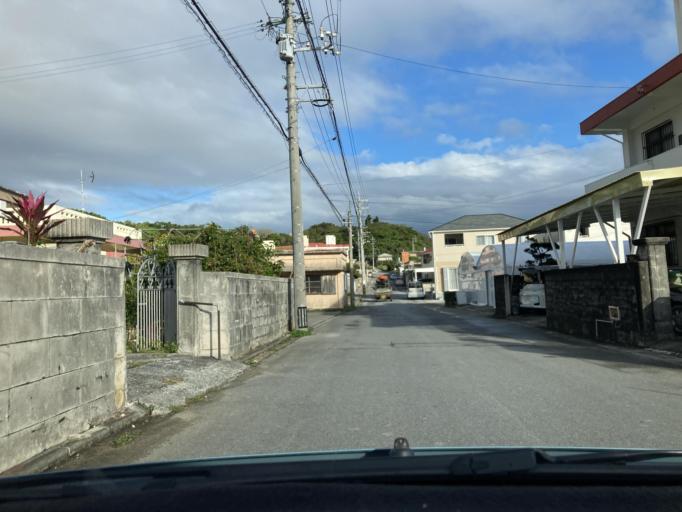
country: JP
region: Okinawa
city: Itoman
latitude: 26.1166
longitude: 127.6718
